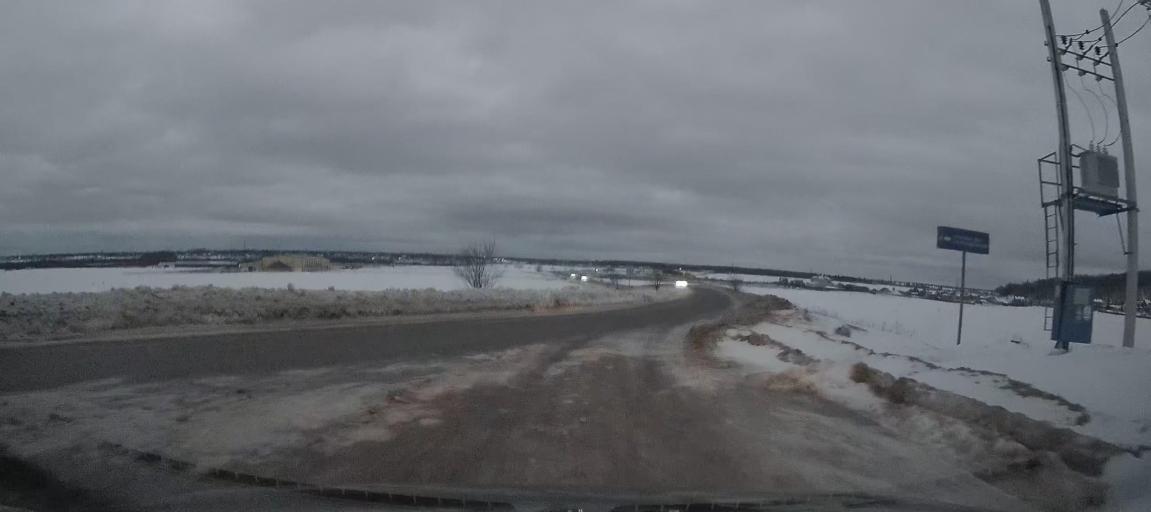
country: RU
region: Leningrad
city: Taytsy
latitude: 59.6924
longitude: 30.1441
